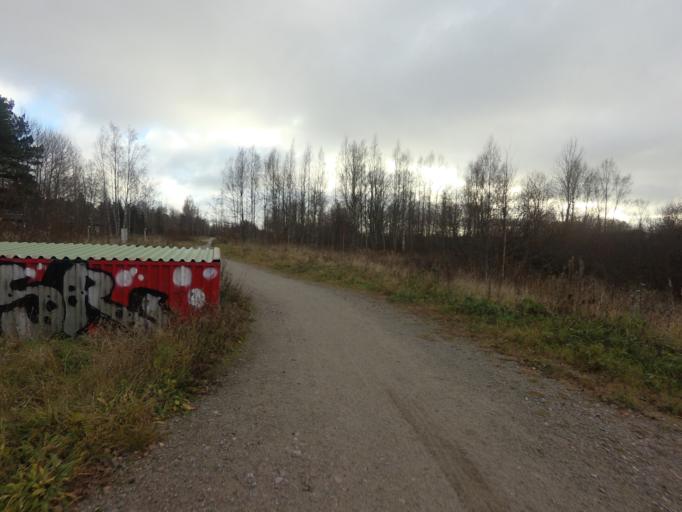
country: FI
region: Uusimaa
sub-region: Helsinki
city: Kauniainen
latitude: 60.1740
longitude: 24.6999
